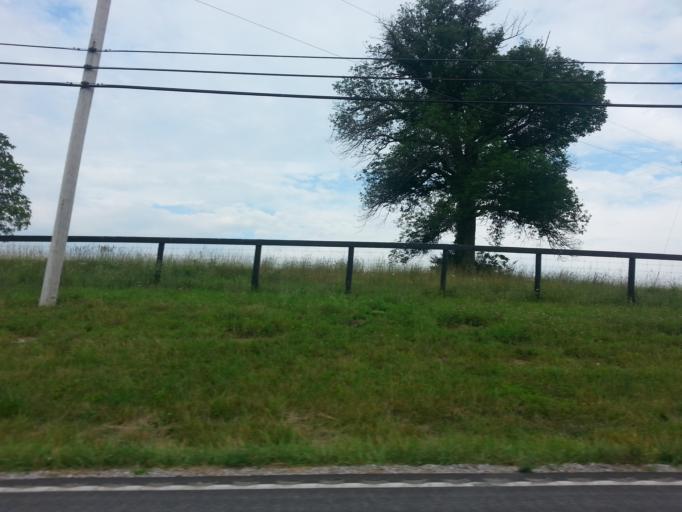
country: US
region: Kentucky
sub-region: Harrison County
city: Cynthiana
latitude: 38.4297
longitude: -84.2543
